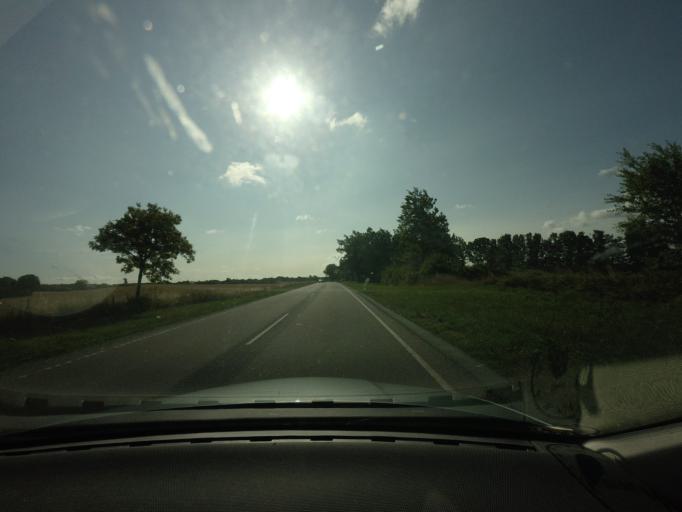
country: DK
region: Zealand
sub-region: Vordingborg Kommune
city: Praesto
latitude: 55.0144
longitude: 12.1147
